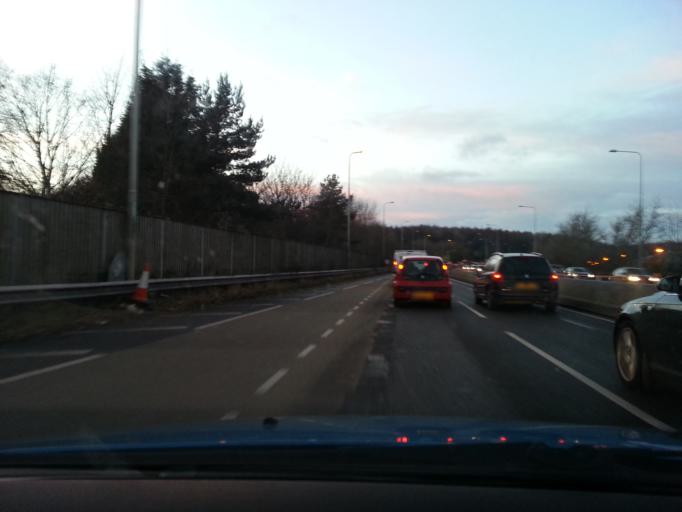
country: GB
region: England
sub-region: Gateshead
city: Lamesley
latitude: 54.9213
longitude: -1.6181
